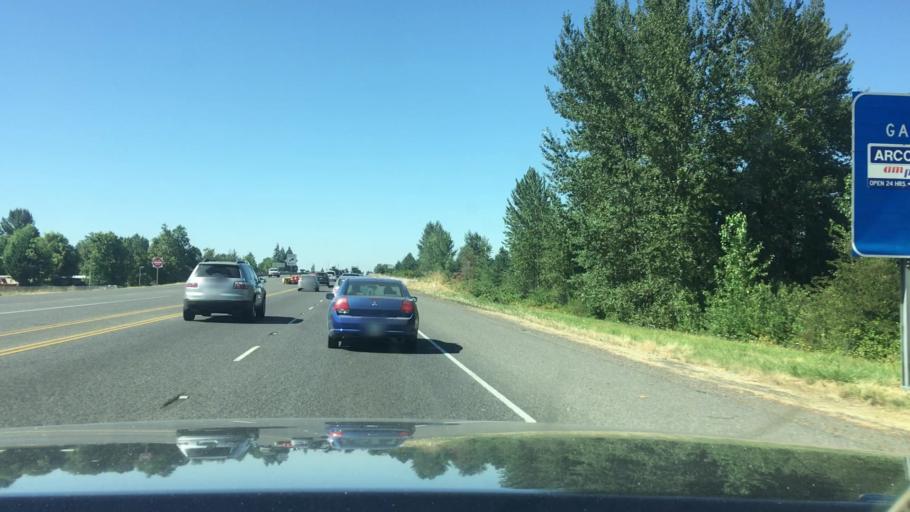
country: US
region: Oregon
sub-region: Lane County
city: Eugene
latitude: 44.0657
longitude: -123.1741
